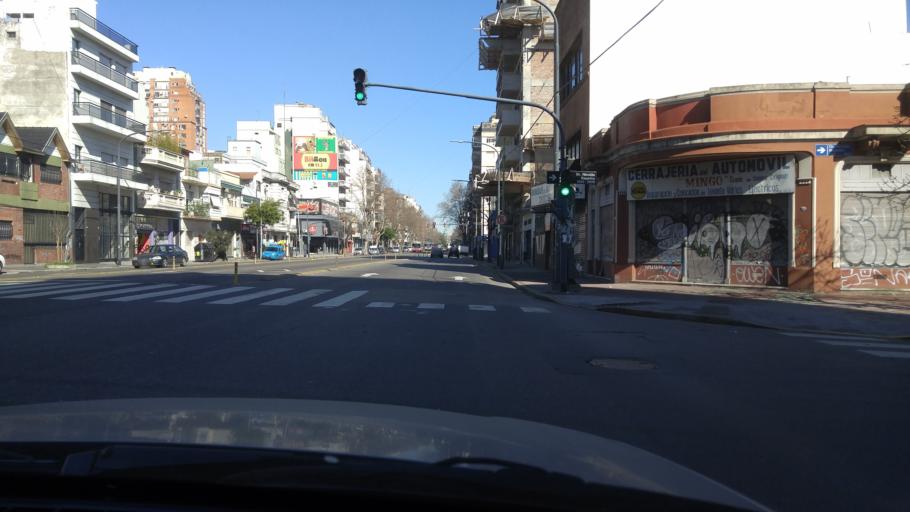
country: AR
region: Buenos Aires F.D.
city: Villa Santa Rita
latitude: -34.6021
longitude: -58.4551
